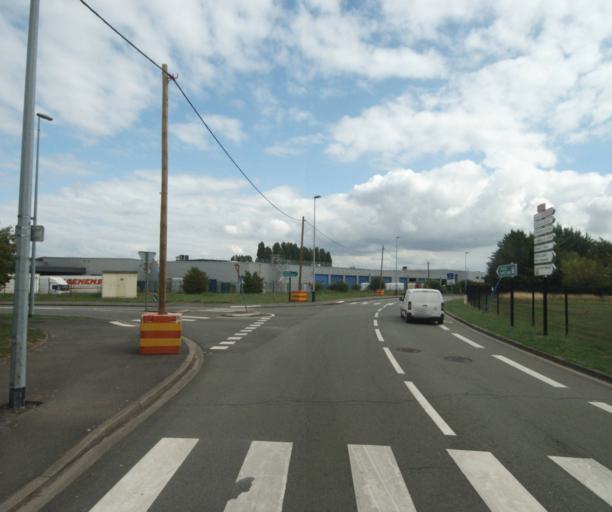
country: FR
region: Nord-Pas-de-Calais
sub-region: Departement du Nord
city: Villeneuve-d'Ascq
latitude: 50.6111
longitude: 3.1515
